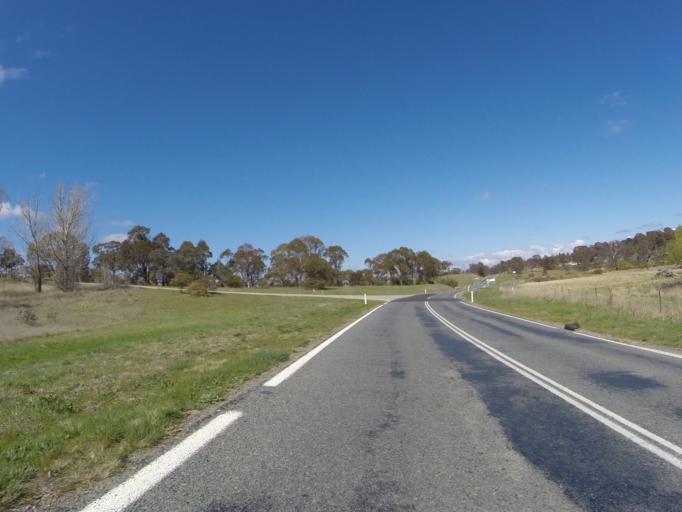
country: AU
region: New South Wales
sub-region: Queanbeyan
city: Queanbeyan
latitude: -35.3190
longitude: 149.2438
